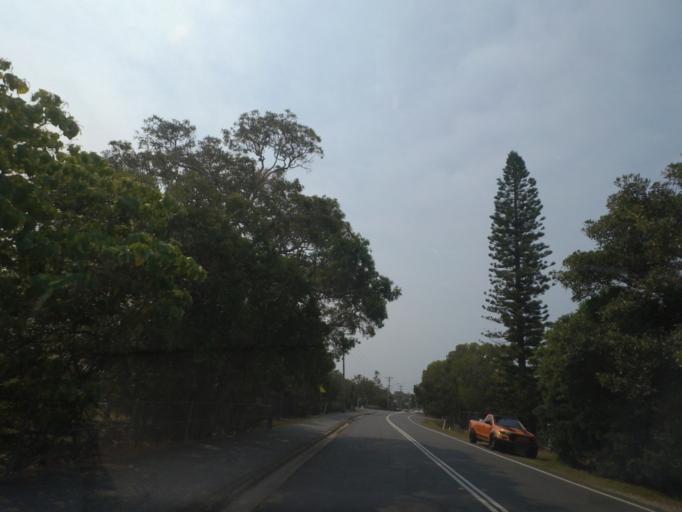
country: AU
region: New South Wales
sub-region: Tweed
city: Pottsville Beach
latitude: -28.3580
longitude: 153.5736
